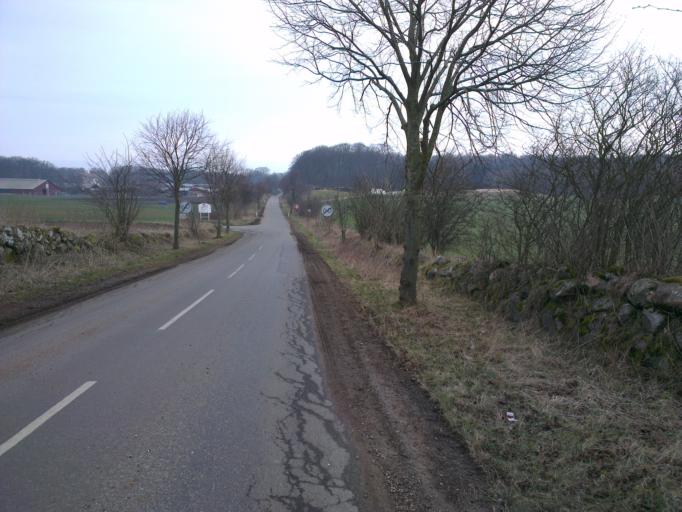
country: DK
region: Capital Region
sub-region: Frederikssund Kommune
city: Skibby
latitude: 55.7773
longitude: 11.9422
